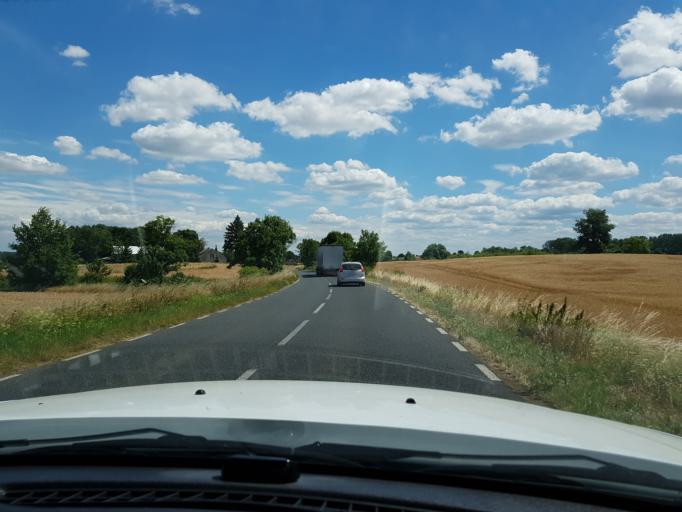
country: PL
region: West Pomeranian Voivodeship
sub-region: Powiat mysliborski
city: Mysliborz
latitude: 52.9063
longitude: 14.9429
